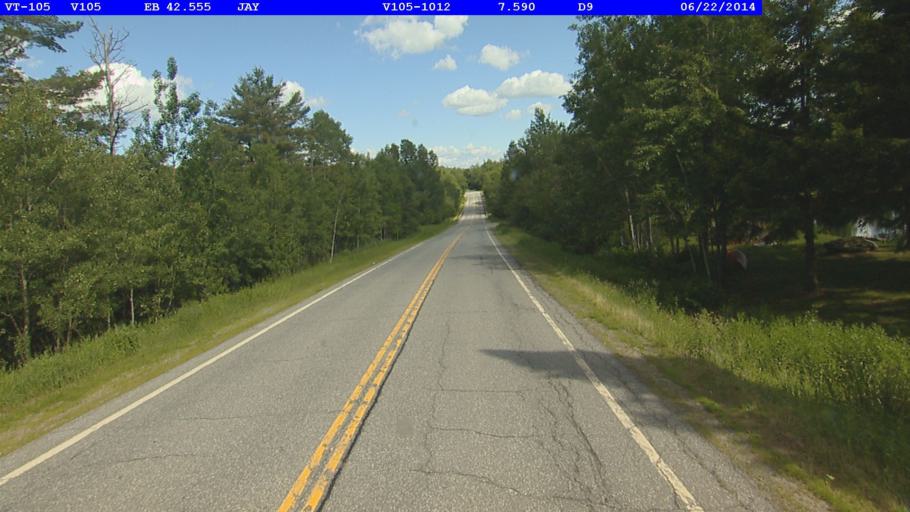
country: CA
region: Quebec
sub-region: Monteregie
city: Sutton
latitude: 44.9668
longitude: -72.4373
